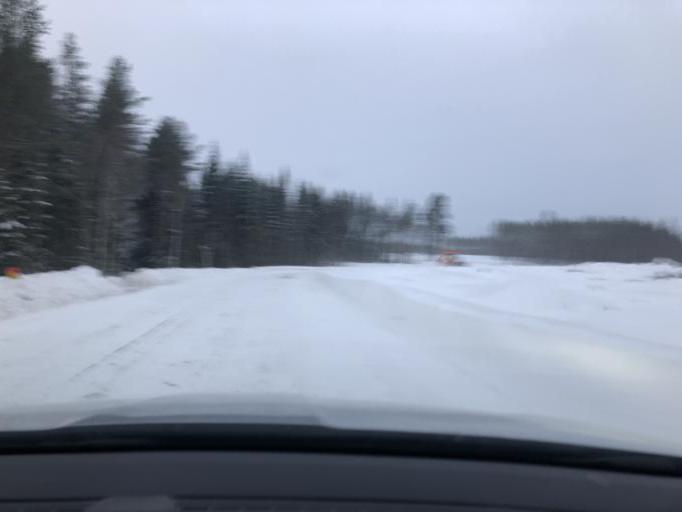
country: SE
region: Vaesterbotten
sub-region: Robertsfors Kommun
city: Robertsfors
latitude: 64.0511
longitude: 20.8481
